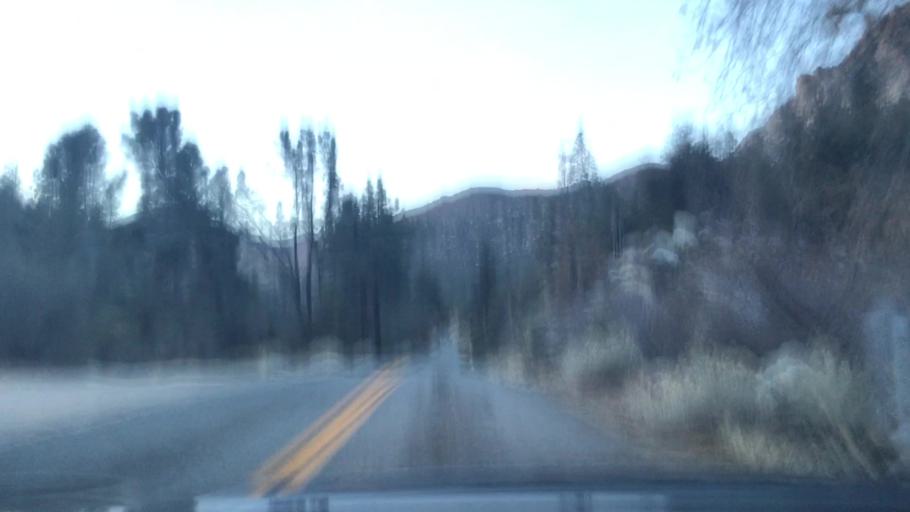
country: US
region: California
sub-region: Kern County
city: Kernville
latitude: 35.8958
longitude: -118.4664
